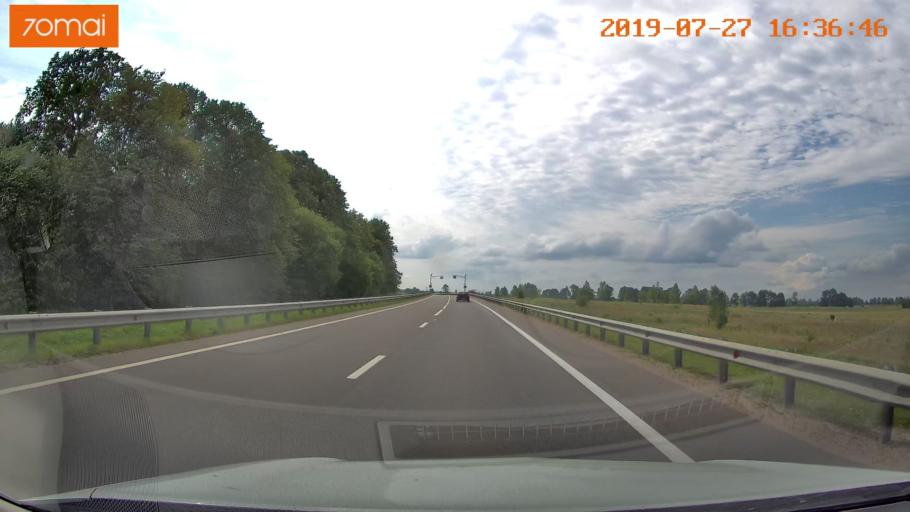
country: RU
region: Kaliningrad
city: Gvardeysk
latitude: 54.6487
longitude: 21.2742
